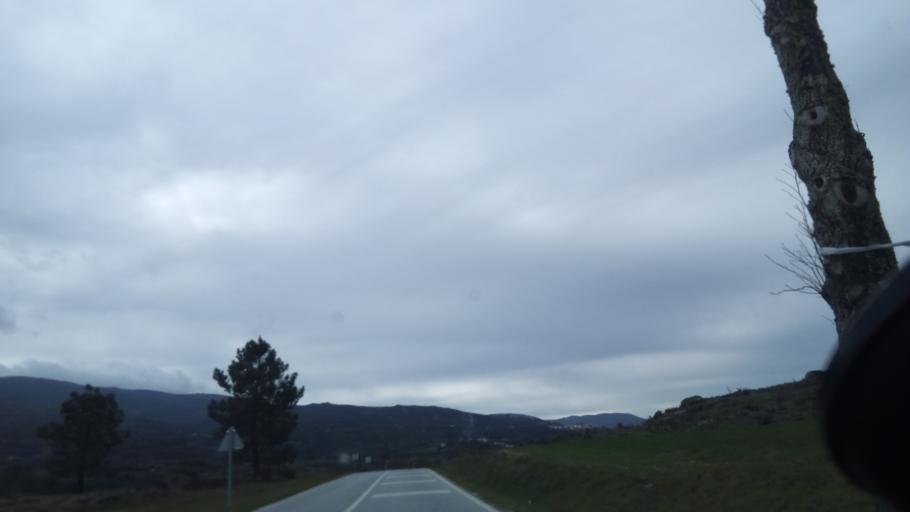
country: PT
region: Guarda
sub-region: Fornos de Algodres
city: Fornos de Algodres
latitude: 40.5378
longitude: -7.5700
